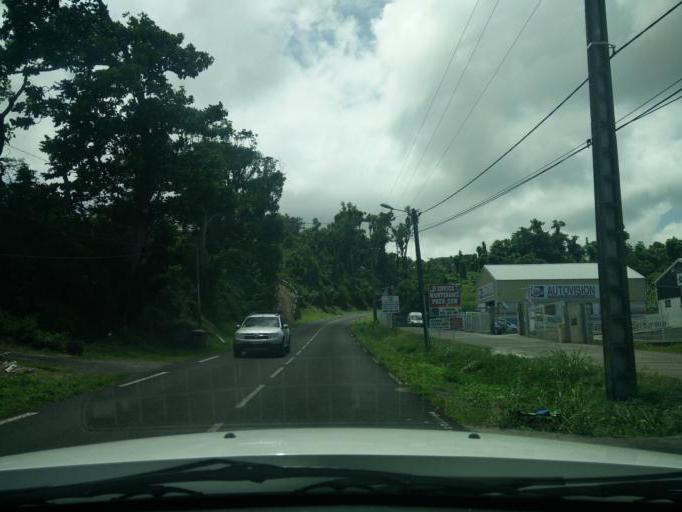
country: GP
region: Guadeloupe
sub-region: Guadeloupe
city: Trois-Rivieres
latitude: 15.9775
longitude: -61.6294
